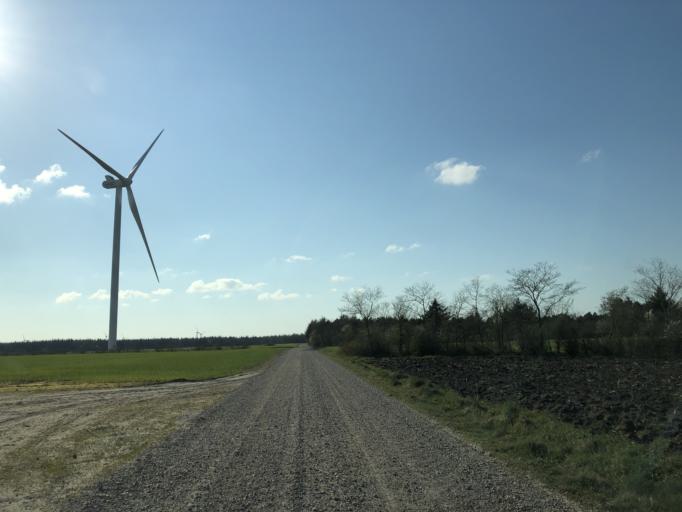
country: DK
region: Central Jutland
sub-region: Holstebro Kommune
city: Ulfborg
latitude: 56.3680
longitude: 8.3213
